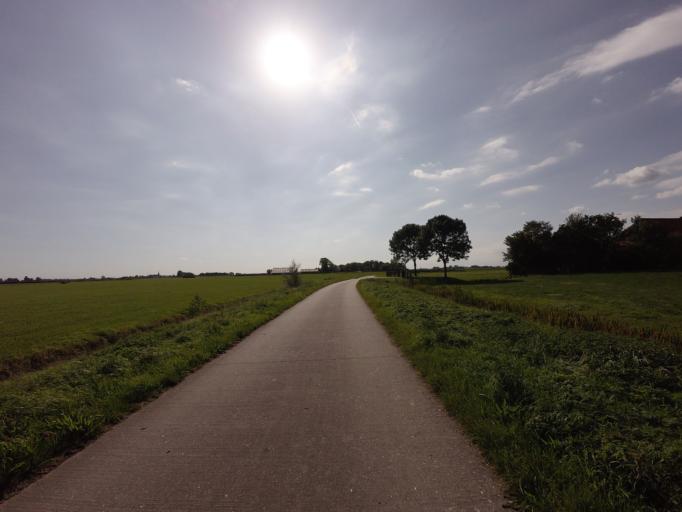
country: NL
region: Friesland
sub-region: Gemeente Littenseradiel
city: Makkum
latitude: 53.0929
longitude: 5.6389
